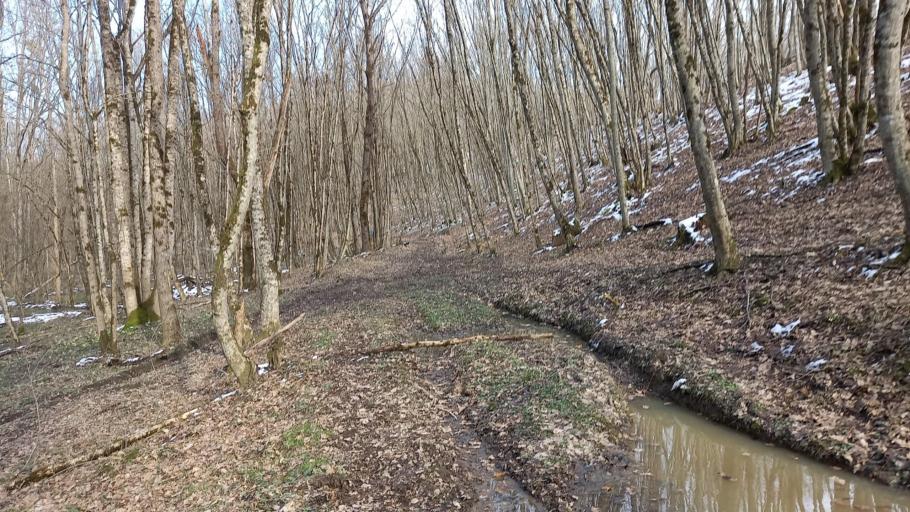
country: RU
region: Krasnodarskiy
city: Smolenskaya
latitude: 44.5961
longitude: 38.8461
